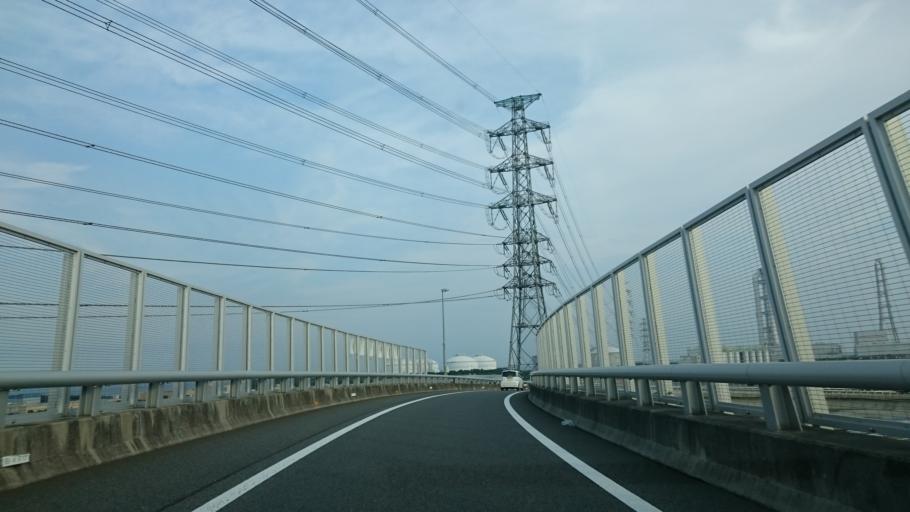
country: JP
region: Mie
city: Yokkaichi
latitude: 35.0211
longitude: 136.6861
